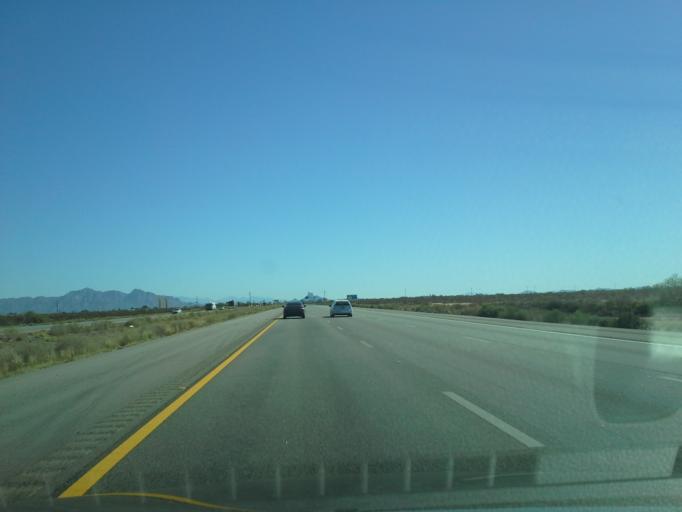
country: US
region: Arizona
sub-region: Pinal County
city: Arizona City
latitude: 32.7925
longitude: -111.6444
